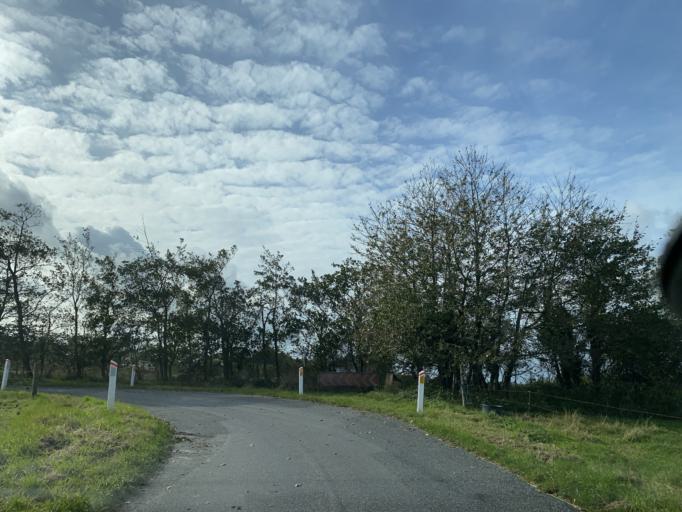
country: DK
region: Central Jutland
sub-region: Arhus Kommune
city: Sabro
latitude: 56.2103
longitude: 9.9987
